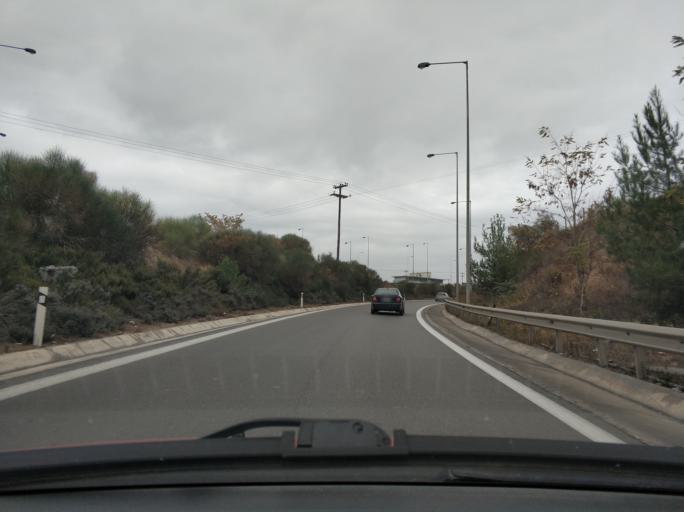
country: GR
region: Central Macedonia
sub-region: Nomos Thessalonikis
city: Efkarpia
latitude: 40.6964
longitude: 22.9498
